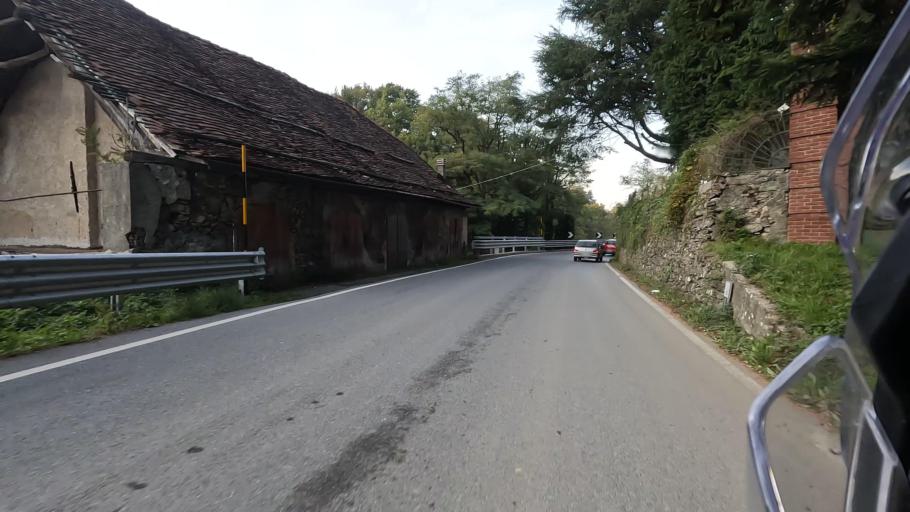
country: IT
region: Liguria
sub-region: Provincia di Savona
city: Sassello
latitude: 44.4651
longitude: 8.4825
